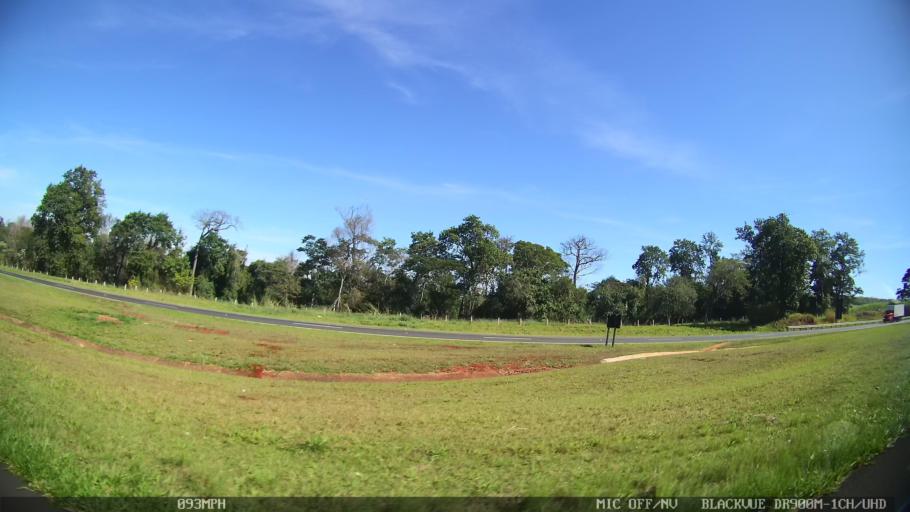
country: BR
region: Sao Paulo
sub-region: Santa Rita Do Passa Quatro
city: Santa Rita do Passa Quatro
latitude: -21.7175
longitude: -47.5896
